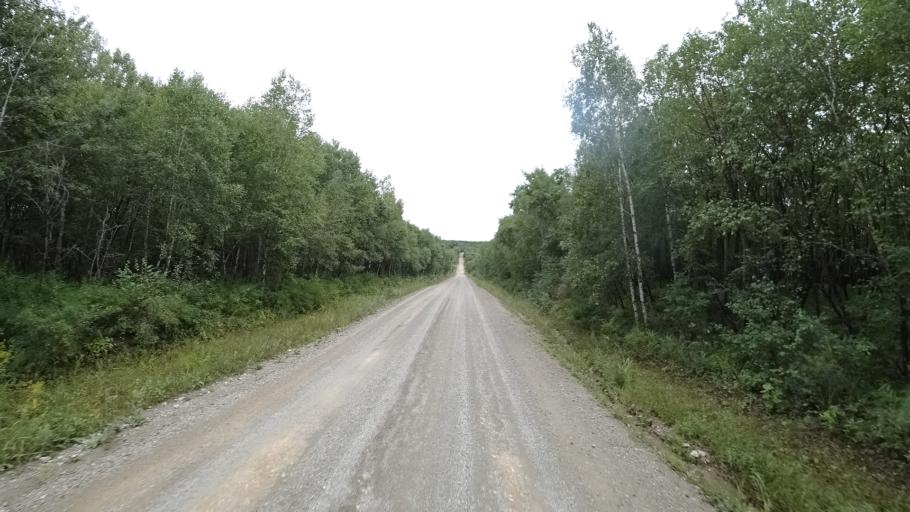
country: RU
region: Primorskiy
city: Ivanovka
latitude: 44.0311
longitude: 132.5076
